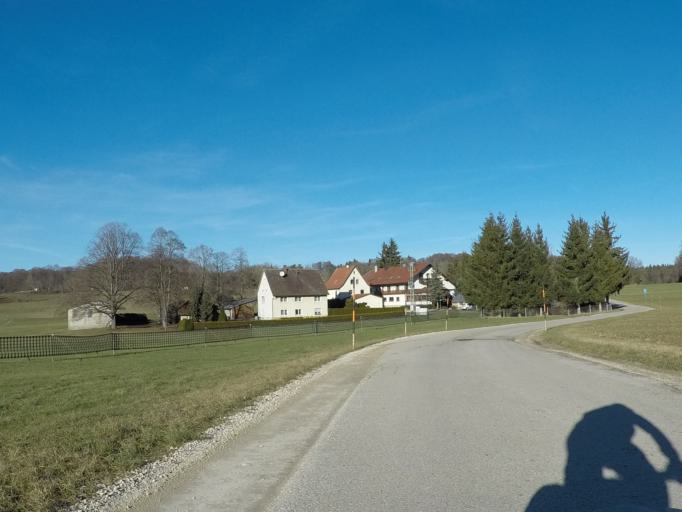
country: DE
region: Baden-Wuerttemberg
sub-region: Tuebingen Region
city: Sankt Johann
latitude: 48.4430
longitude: 9.3043
